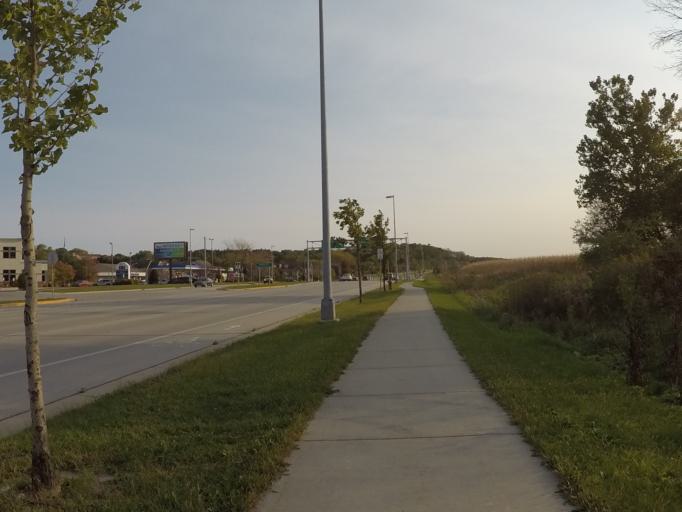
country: US
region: Wisconsin
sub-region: Dane County
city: Middleton
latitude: 43.0577
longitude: -89.5279
